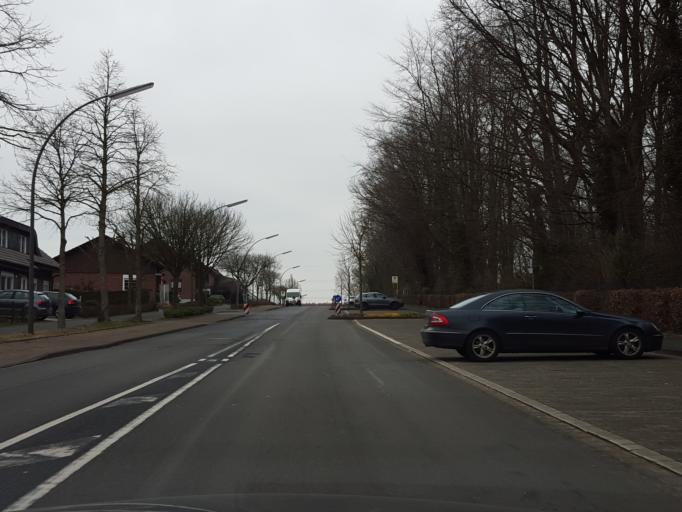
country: DE
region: North Rhine-Westphalia
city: Oer-Erkenschwick
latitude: 51.6544
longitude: 7.2514
